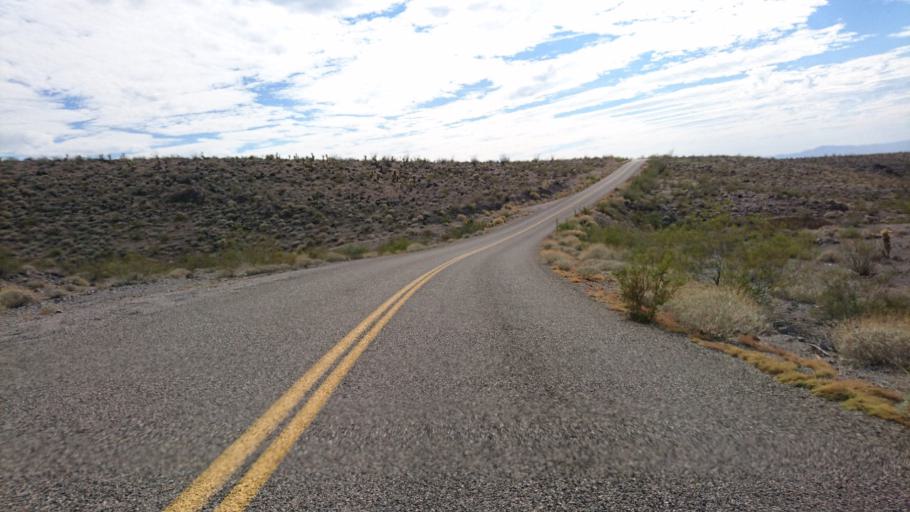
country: US
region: Arizona
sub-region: Mohave County
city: Mohave Valley
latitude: 34.9610
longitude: -114.4086
